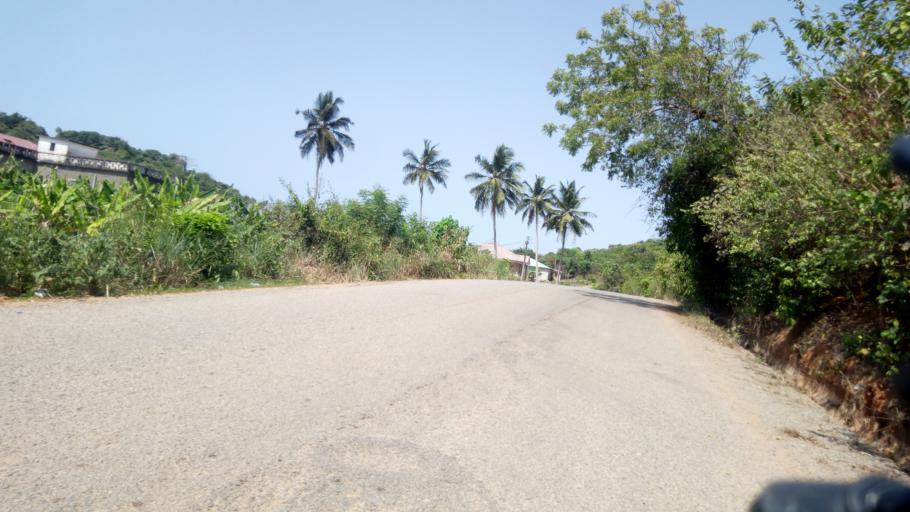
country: GH
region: Central
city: Cape Coast
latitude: 5.1085
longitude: -1.2716
